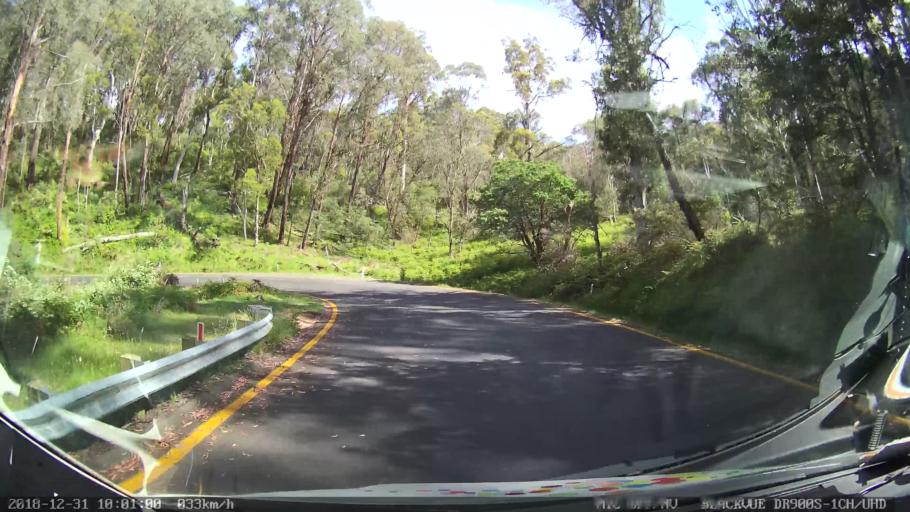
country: AU
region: New South Wales
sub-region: Snowy River
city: Jindabyne
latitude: -36.5299
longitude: 148.2045
